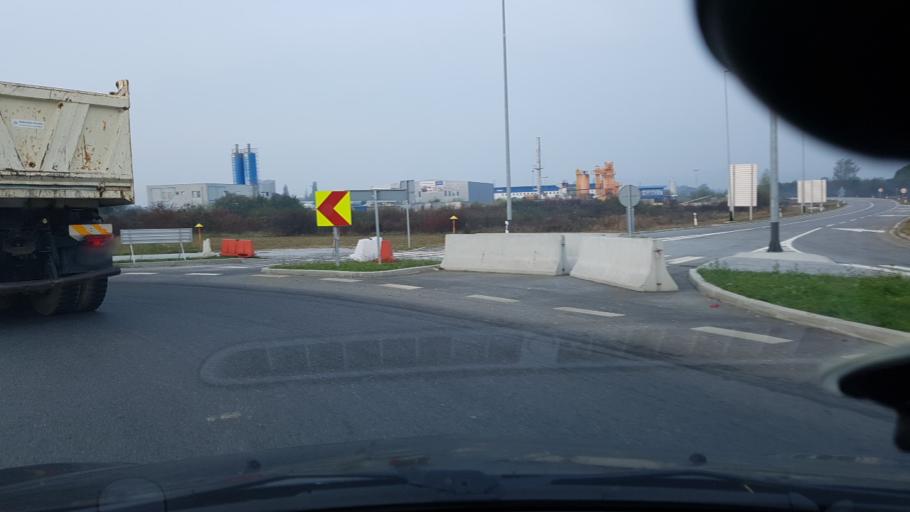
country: HR
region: Krapinsko-Zagorska
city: Oroslavje
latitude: 46.0098
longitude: 15.8759
